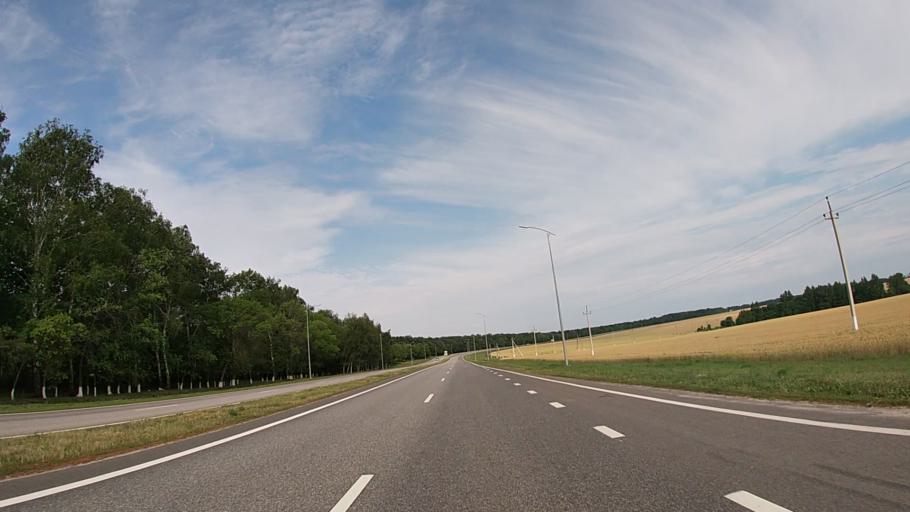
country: RU
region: Belgorod
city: Borisovka
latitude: 50.7511
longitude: 35.9790
